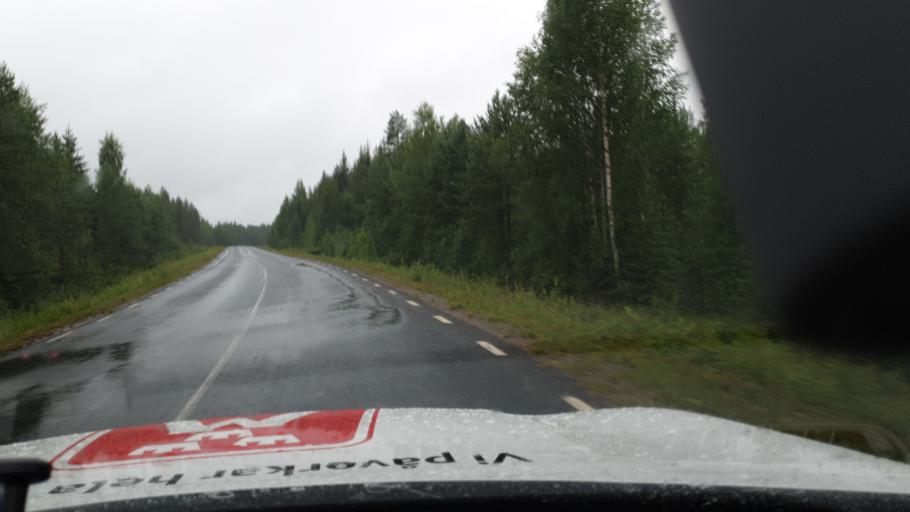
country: SE
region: Vaesterbotten
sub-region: Skelleftea Kommun
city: Soedra Bergsbyn
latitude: 64.5925
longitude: 21.0527
